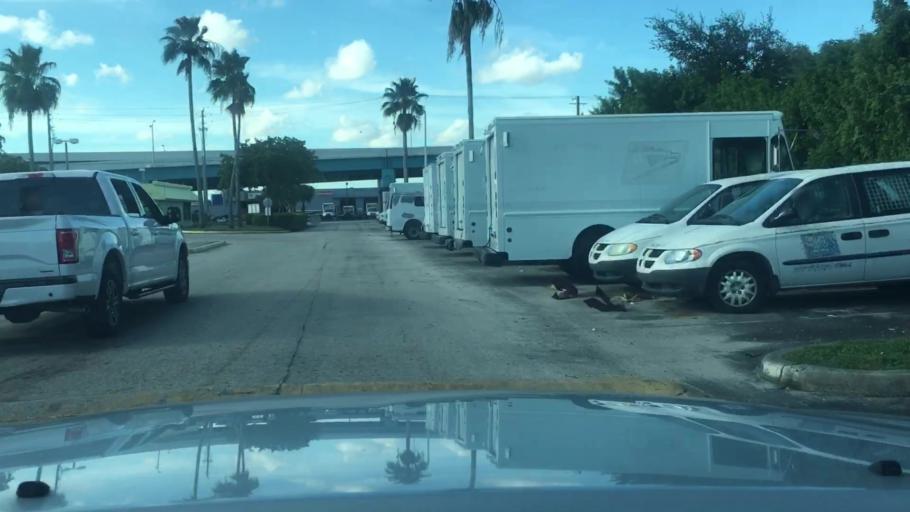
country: US
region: Florida
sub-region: Miami-Dade County
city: Virginia Gardens
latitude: 25.7958
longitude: -80.3179
